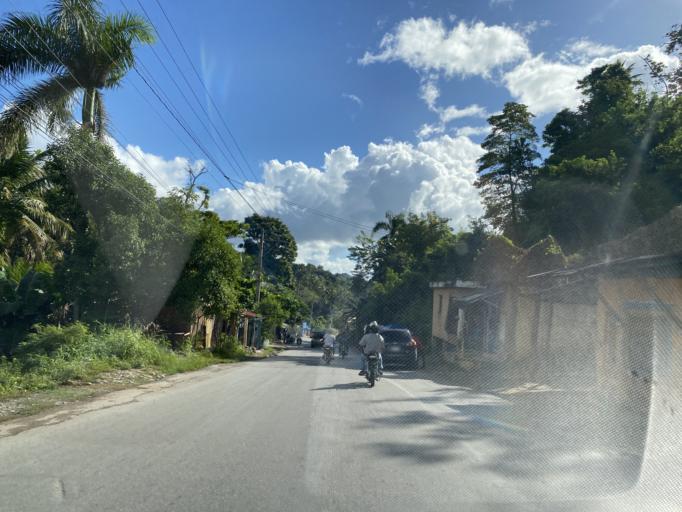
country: DO
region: Samana
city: Samana
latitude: 19.2072
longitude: -69.3512
